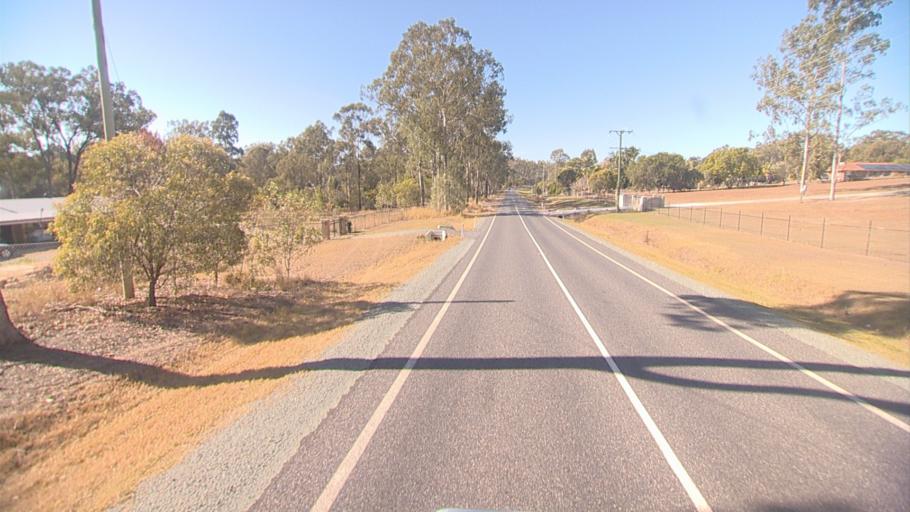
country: AU
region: Queensland
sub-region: Logan
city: Cedar Vale
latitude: -27.8530
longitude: 153.0326
